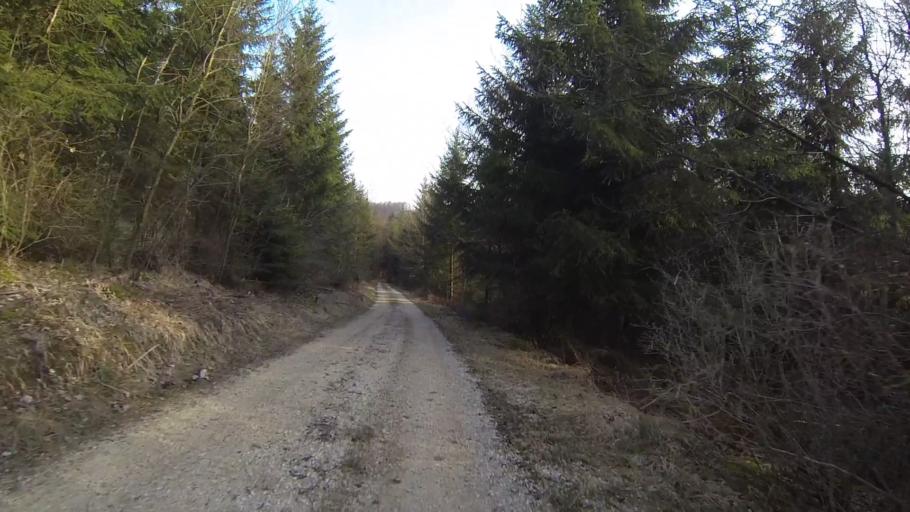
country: DE
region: Baden-Wuerttemberg
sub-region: Regierungsbezirk Stuttgart
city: Bolheim
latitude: 48.6530
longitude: 10.1123
